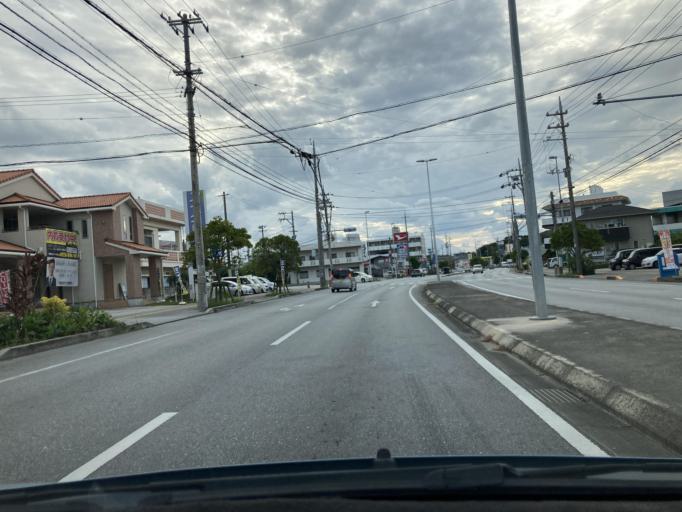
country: JP
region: Okinawa
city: Okinawa
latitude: 26.3592
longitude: 127.8088
